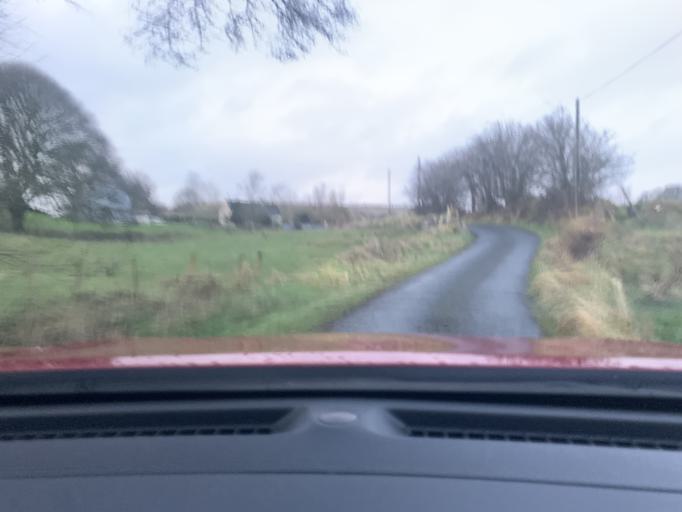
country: IE
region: Connaught
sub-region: Sligo
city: Ballymote
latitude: 54.0461
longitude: -8.4070
